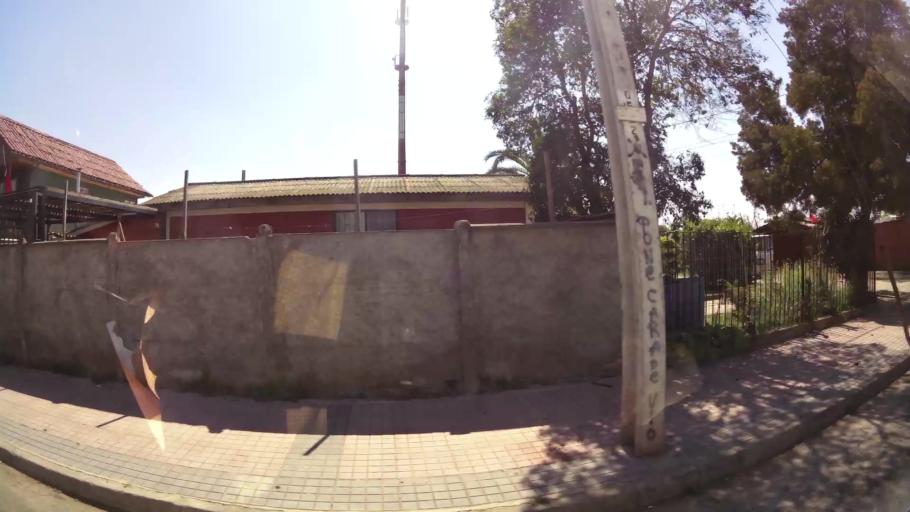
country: CL
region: Santiago Metropolitan
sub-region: Provincia de Talagante
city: Talagante
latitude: -33.6589
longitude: -70.9200
